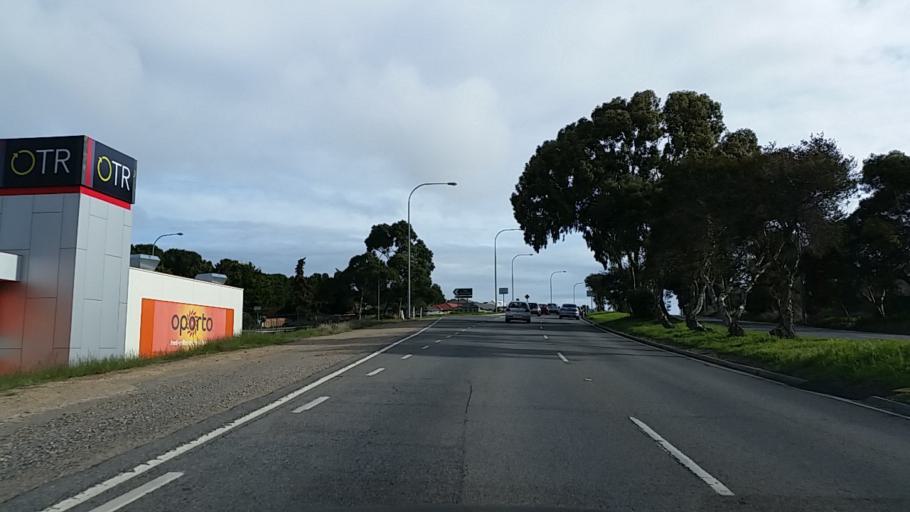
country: AU
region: South Australia
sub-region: Onkaparinga
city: Reynella
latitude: -35.0960
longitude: 138.5361
